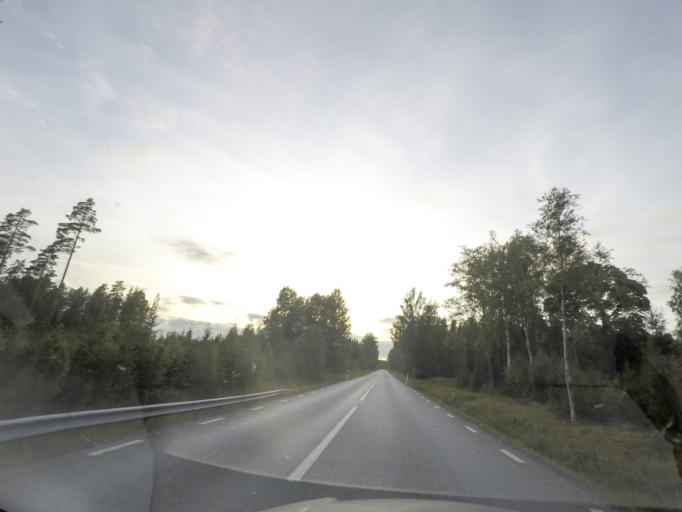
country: SE
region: OErebro
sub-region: Hallefors Kommun
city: Haellefors
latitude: 59.5920
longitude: 14.6857
